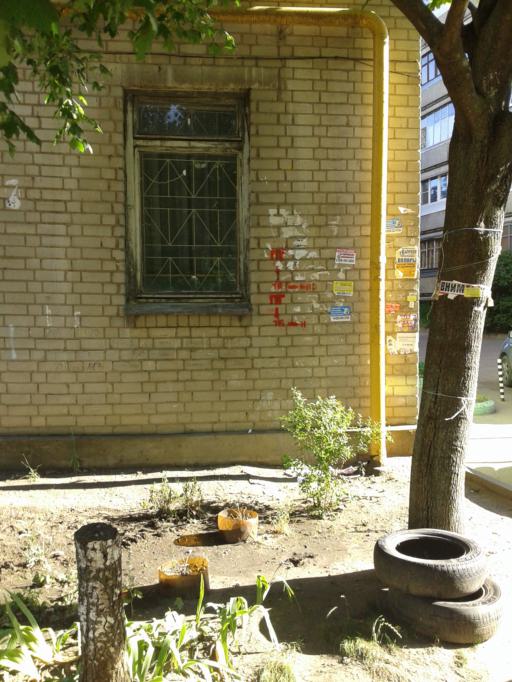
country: RU
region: Voronezj
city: Voronezh
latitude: 51.6554
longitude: 39.1290
